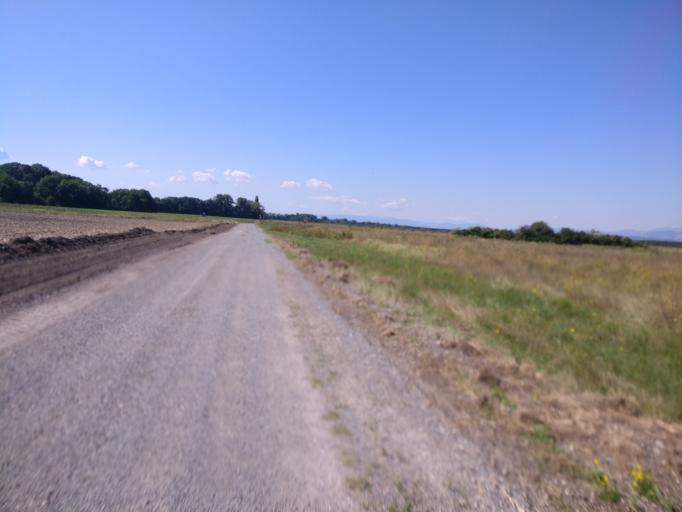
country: AT
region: Lower Austria
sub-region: Politischer Bezirk Baden
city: Pottendorf
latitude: 47.9184
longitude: 16.3594
